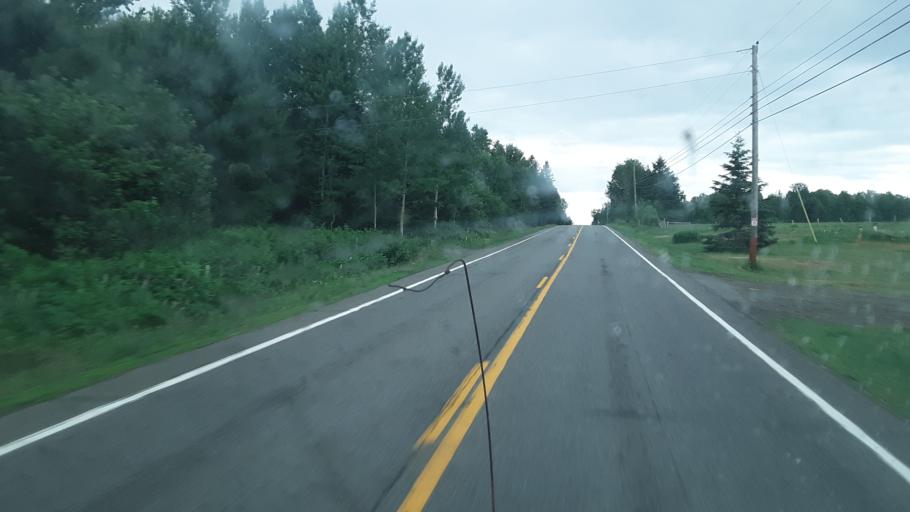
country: US
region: Maine
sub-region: Aroostook County
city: Presque Isle
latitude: 46.4879
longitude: -68.3787
